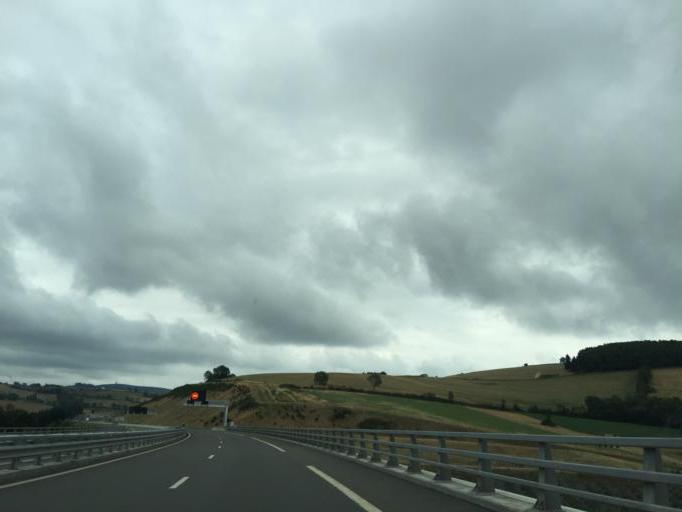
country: FR
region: Rhone-Alpes
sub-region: Departement de la Loire
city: Bussieres
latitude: 45.8630
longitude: 4.3094
